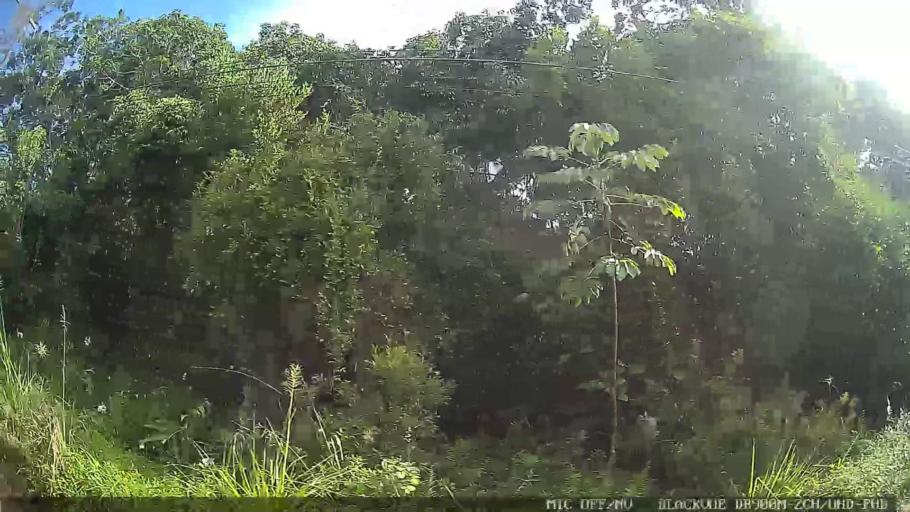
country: BR
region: Sao Paulo
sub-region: Itanhaem
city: Itanhaem
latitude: -24.2077
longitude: -46.8812
